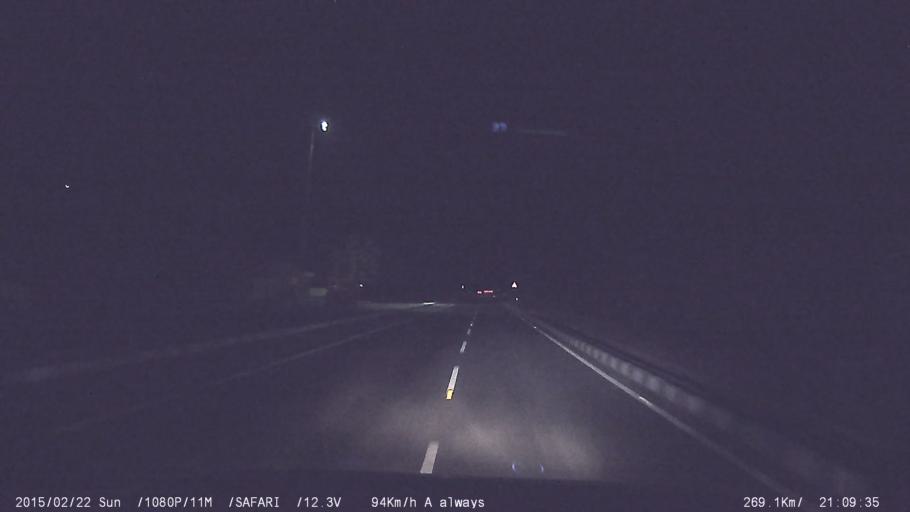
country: IN
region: Tamil Nadu
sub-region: Karur
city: Pallappatti
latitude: 10.7481
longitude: 77.9159
